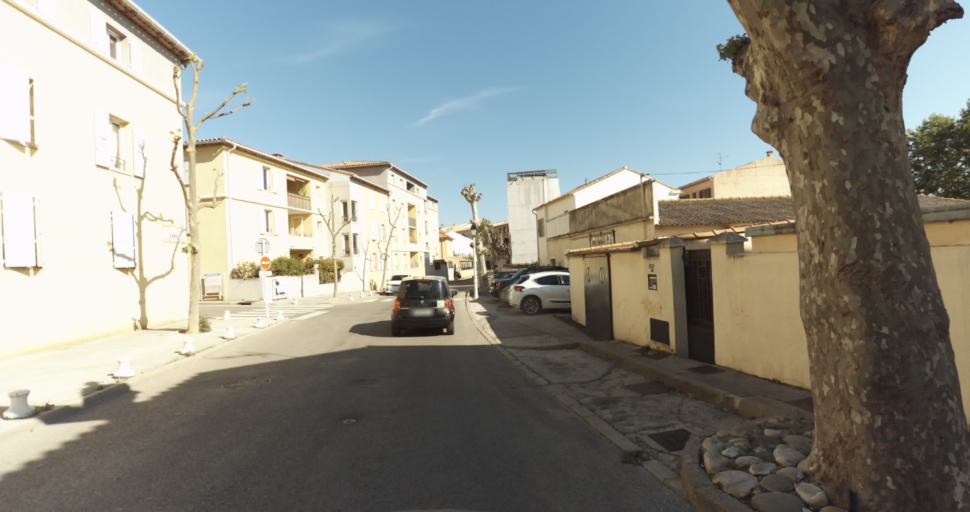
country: FR
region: Provence-Alpes-Cote d'Azur
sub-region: Departement du Var
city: Carqueiranne
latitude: 43.0957
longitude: 6.0706
